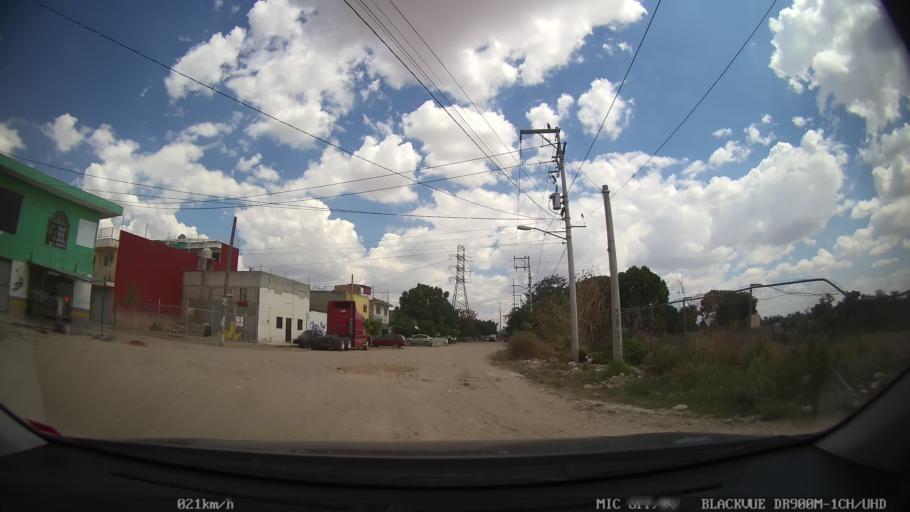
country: MX
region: Jalisco
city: Tlaquepaque
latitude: 20.6743
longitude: -103.2619
